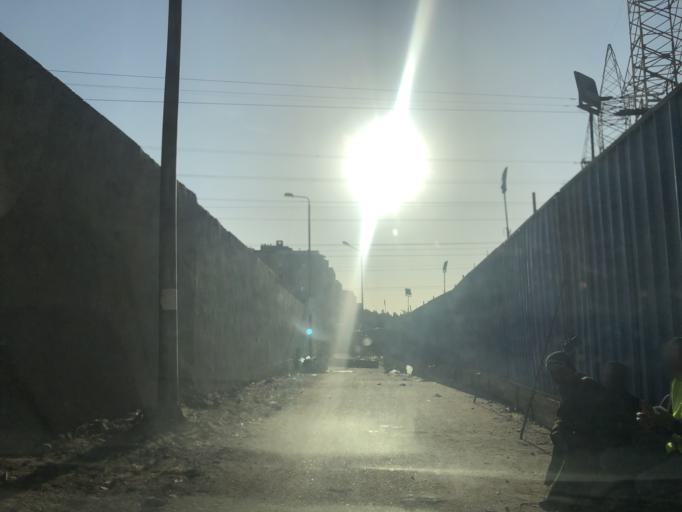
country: EG
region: Al Jizah
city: Al Jizah
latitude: 29.9883
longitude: 31.0967
